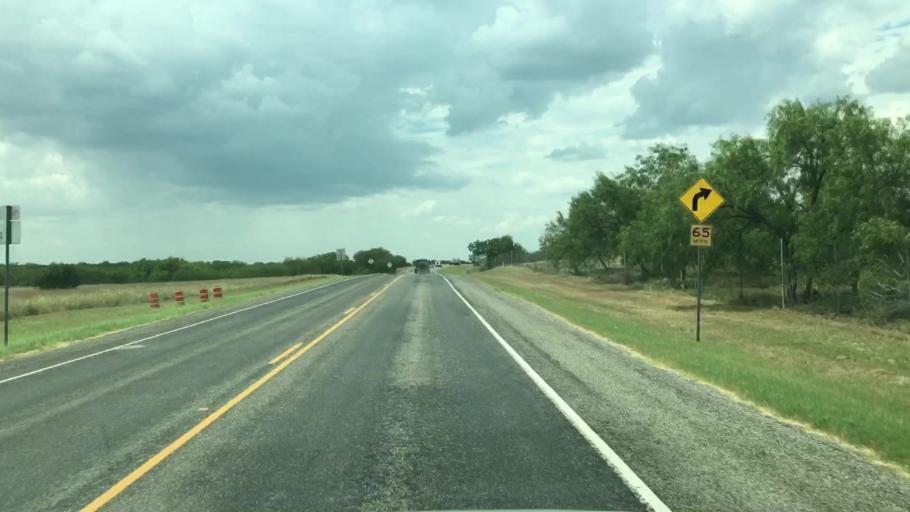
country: US
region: Texas
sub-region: Live Oak County
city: Three Rivers
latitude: 28.6390
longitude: -98.2794
